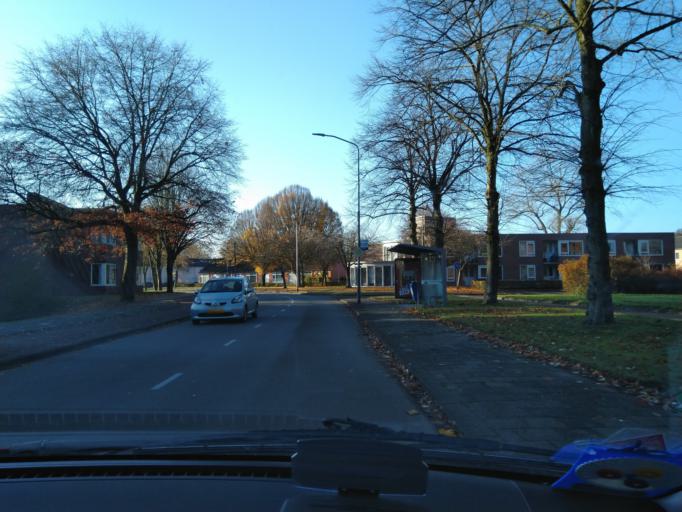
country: NL
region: Drenthe
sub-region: Gemeente Assen
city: Assen
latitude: 53.0045
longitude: 6.5491
